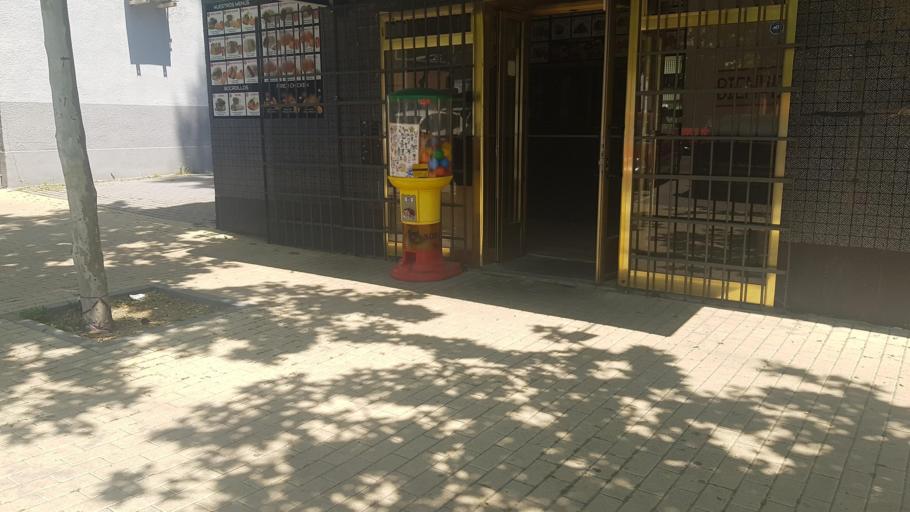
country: ES
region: Madrid
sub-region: Provincia de Madrid
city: Villaverde
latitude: 40.3590
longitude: -3.6960
